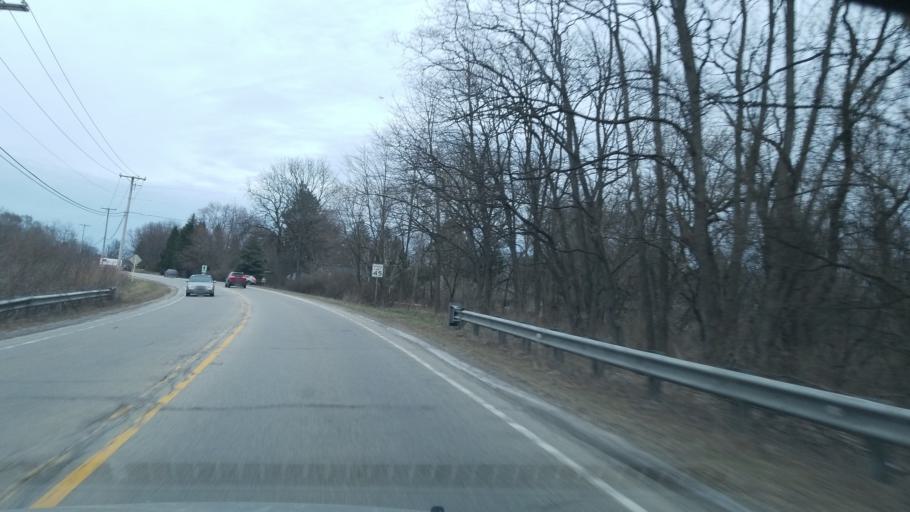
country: US
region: Illinois
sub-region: Kane County
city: Sleepy Hollow
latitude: 42.1013
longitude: -88.3127
